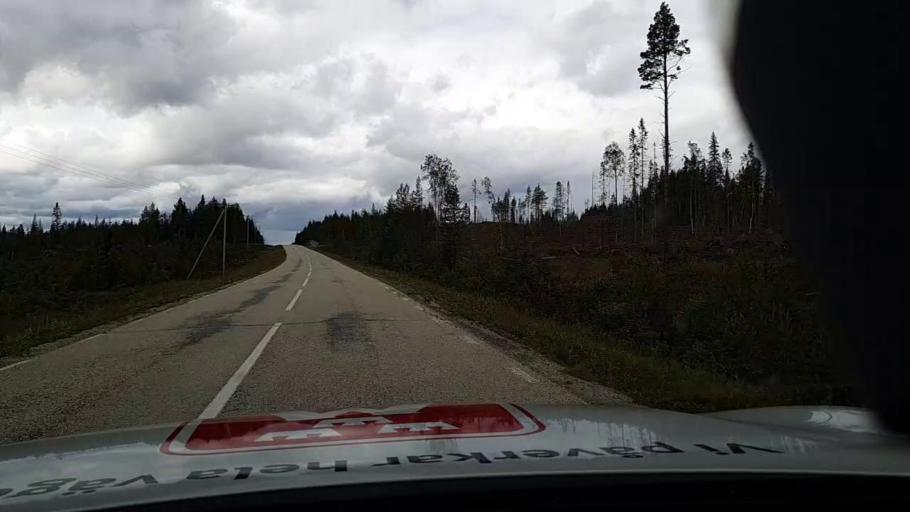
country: SE
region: Jaemtland
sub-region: Are Kommun
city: Jarpen
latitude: 62.7676
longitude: 13.7234
